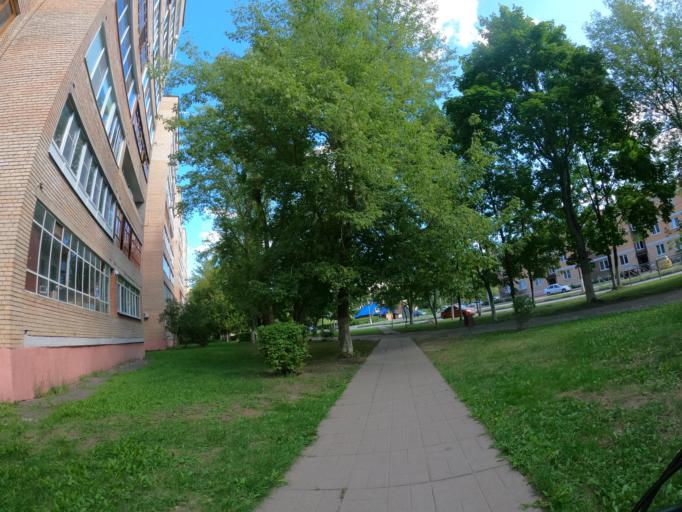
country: RU
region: Moskovskaya
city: Stupino
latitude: 54.8853
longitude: 38.0556
